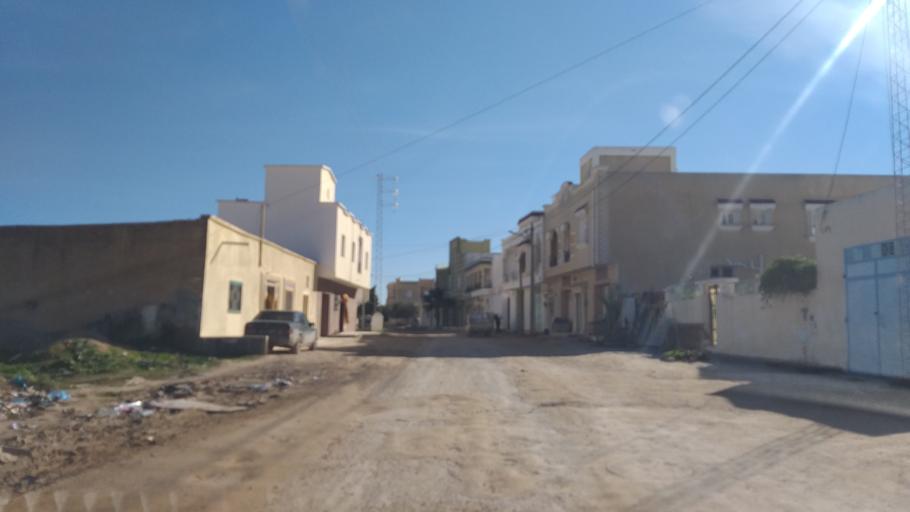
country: TN
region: Al Mahdiyah
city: El Jem
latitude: 35.2933
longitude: 10.7158
